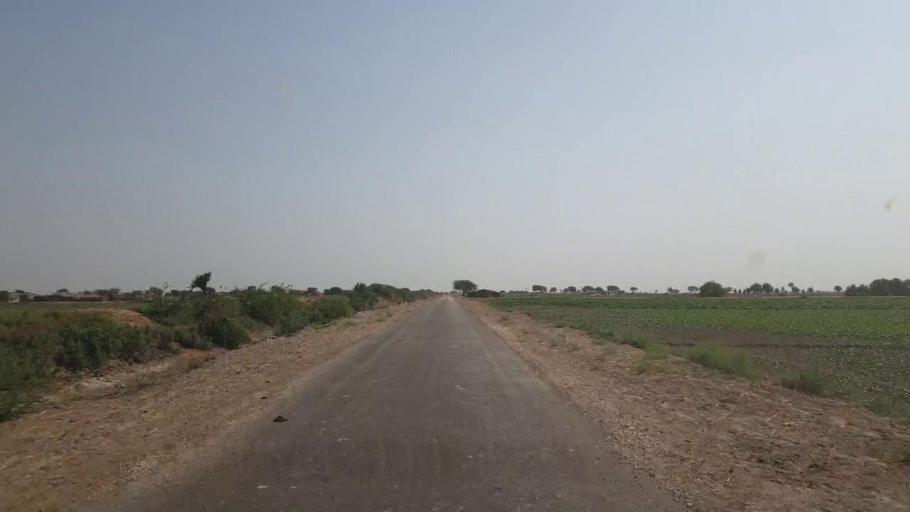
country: PK
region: Sindh
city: Jati
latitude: 24.4532
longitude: 68.5145
